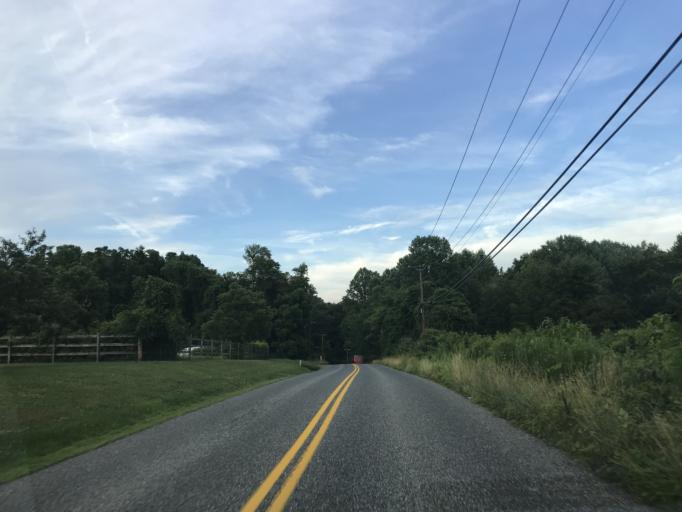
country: US
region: Maryland
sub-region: Harford County
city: Aberdeen
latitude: 39.5155
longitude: -76.2014
